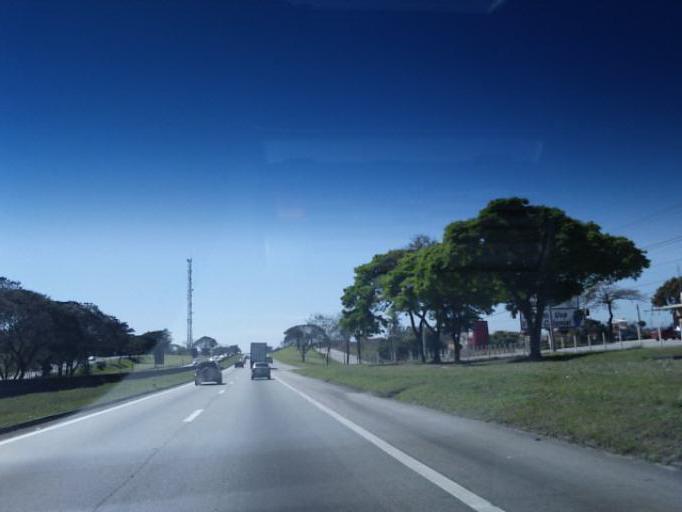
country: BR
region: Sao Paulo
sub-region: Cacapava
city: Cacapava
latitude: -23.1230
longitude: -45.7276
